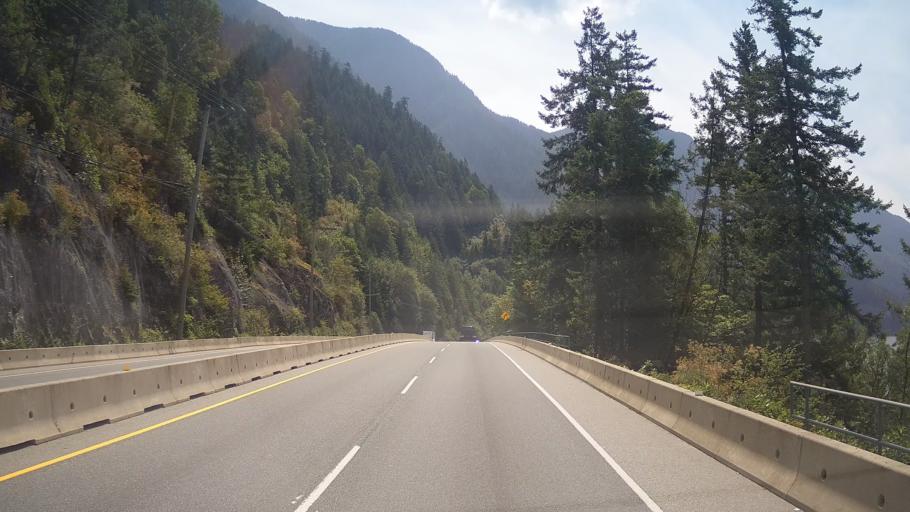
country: CA
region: British Columbia
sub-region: Greater Vancouver Regional District
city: Lions Bay
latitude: 49.4353
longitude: -123.2353
